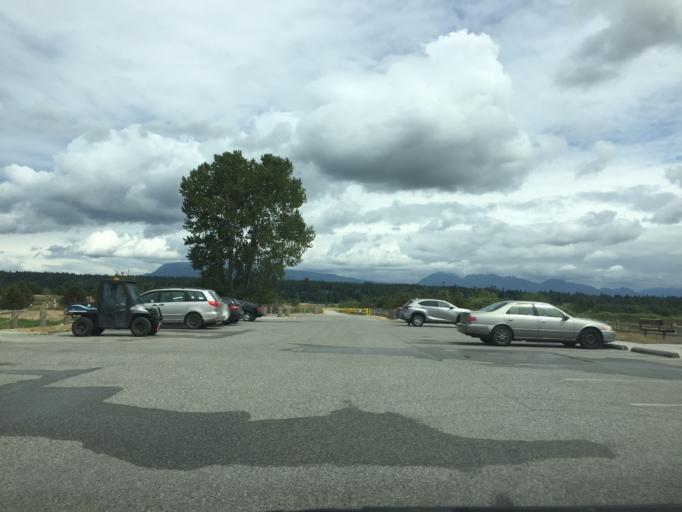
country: CA
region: British Columbia
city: Richmond
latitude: 49.2187
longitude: -123.2134
